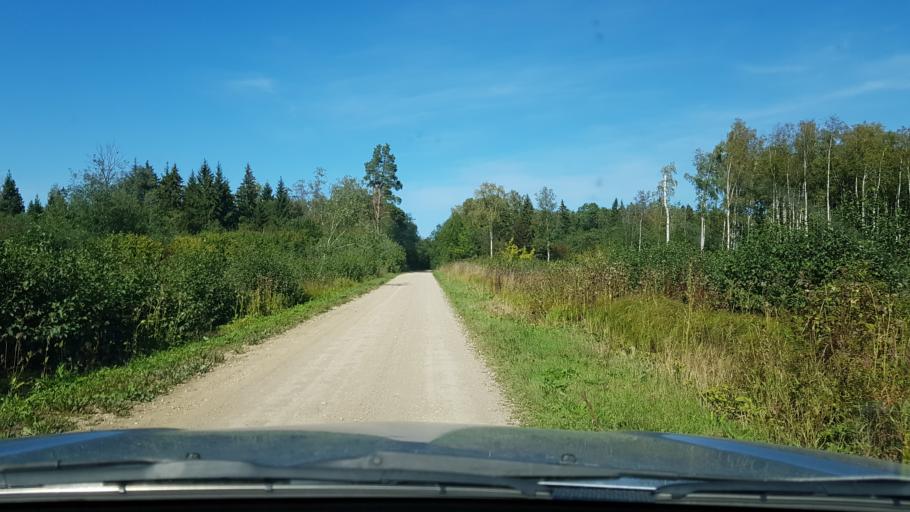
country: EE
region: Ida-Virumaa
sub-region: Sillamaee linn
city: Sillamae
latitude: 59.3841
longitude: 27.8547
